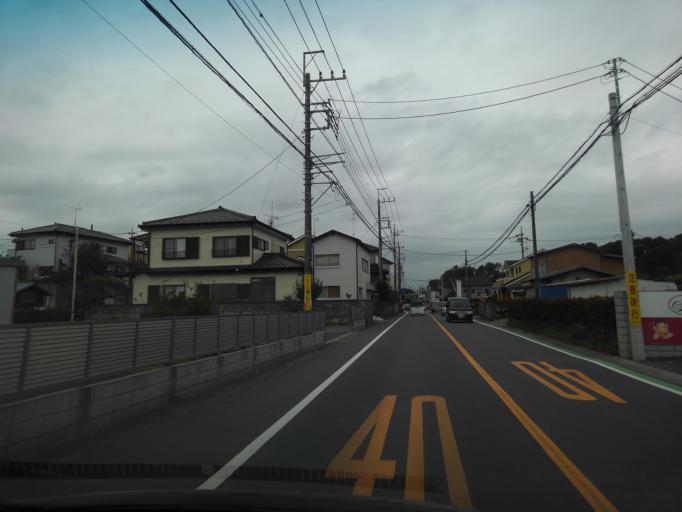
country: JP
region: Saitama
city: Tokorozawa
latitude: 35.7896
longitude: 139.4182
